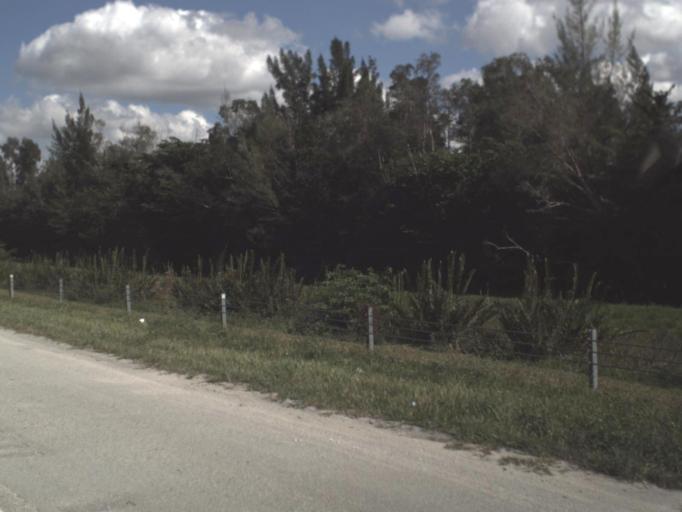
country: US
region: Florida
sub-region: Miami-Dade County
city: Palm Springs North
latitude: 25.9148
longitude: -80.3800
